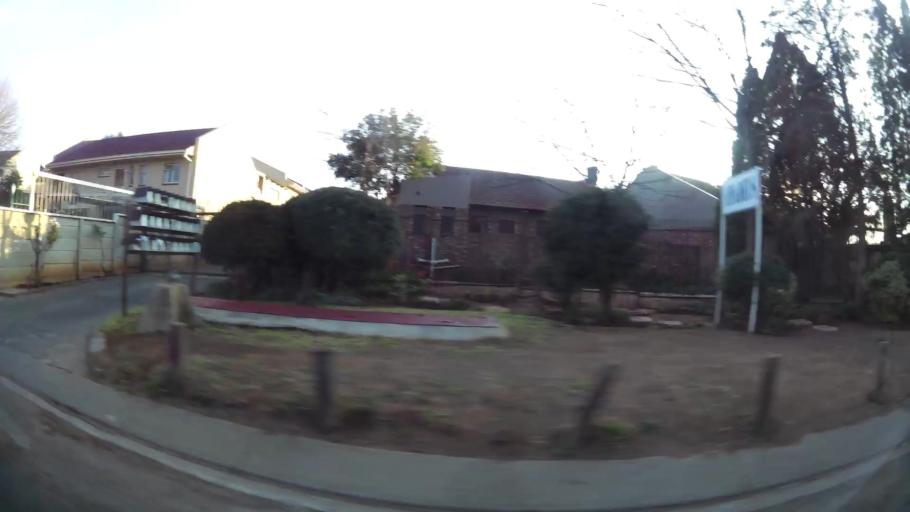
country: ZA
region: Orange Free State
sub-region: Mangaung Metropolitan Municipality
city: Bloemfontein
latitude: -29.0956
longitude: 26.1576
